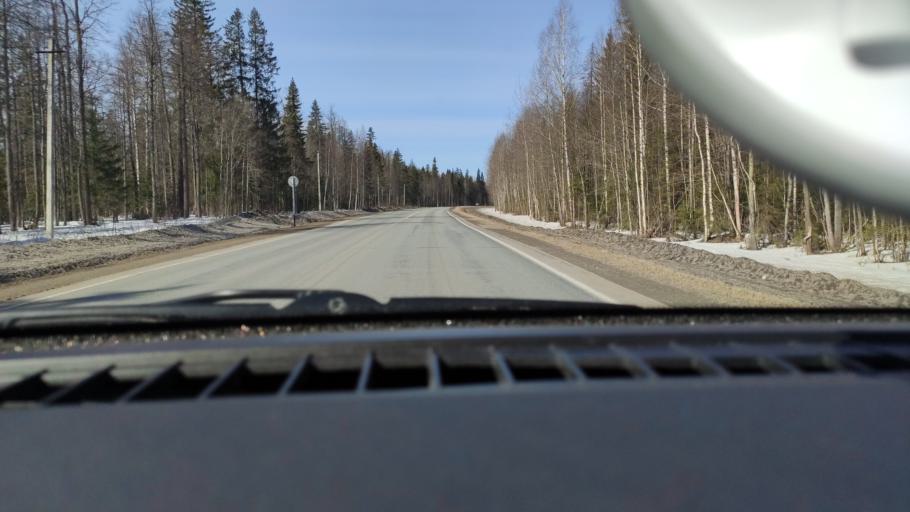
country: RU
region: Perm
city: Perm
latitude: 58.2141
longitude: 56.1777
